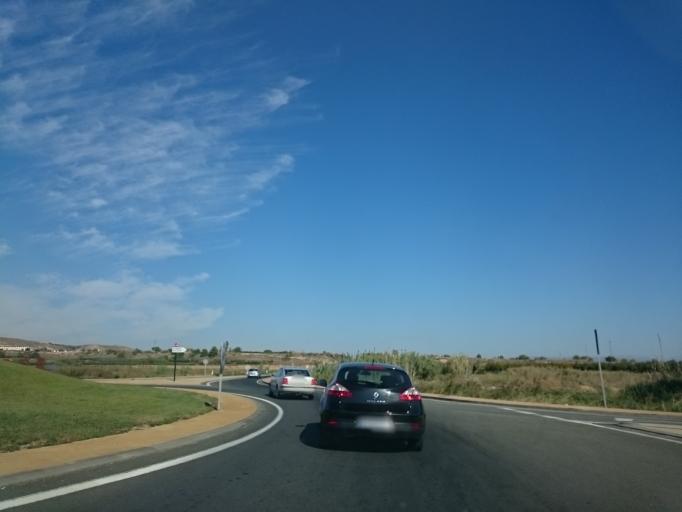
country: ES
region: Catalonia
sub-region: Provincia de Lleida
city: Torrefarrera
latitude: 41.7010
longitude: 0.5958
